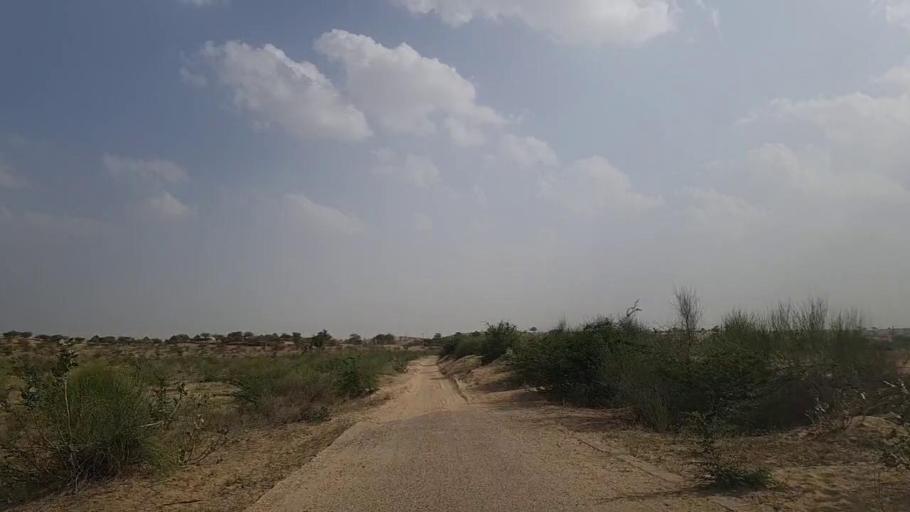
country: PK
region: Sindh
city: Islamkot
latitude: 24.8749
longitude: 70.1639
